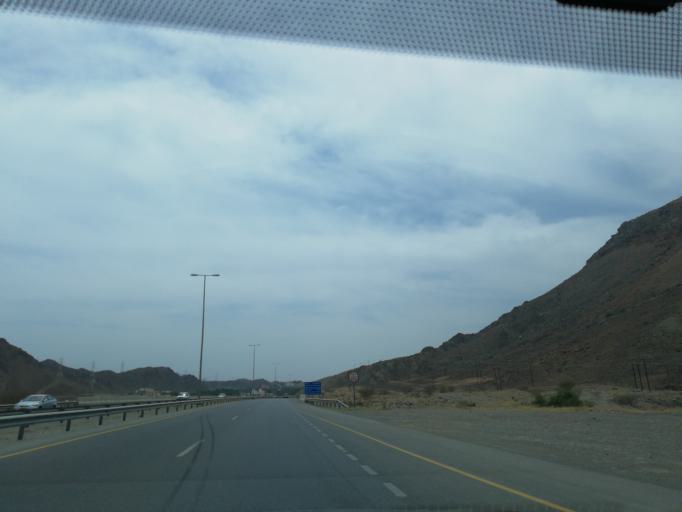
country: OM
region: Muhafazat ad Dakhiliyah
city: Izki
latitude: 23.1301
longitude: 57.8404
